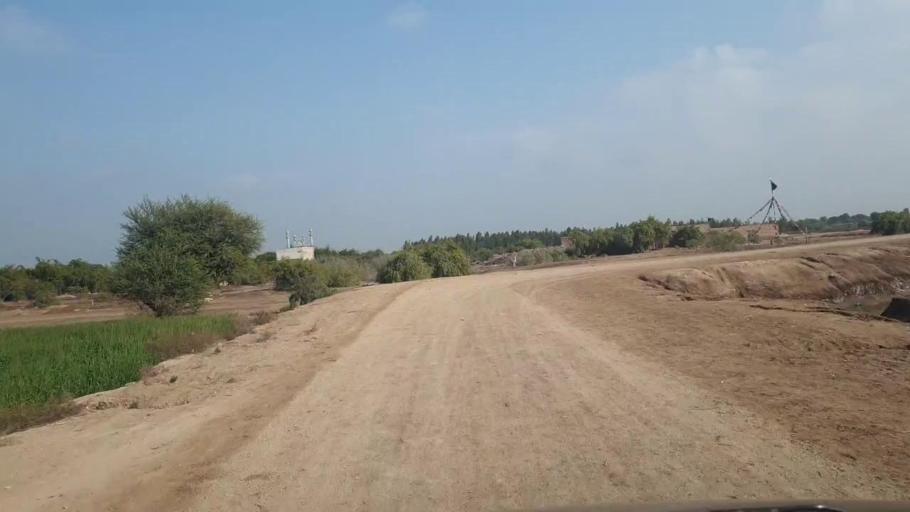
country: PK
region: Sindh
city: Shahdadpur
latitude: 25.9132
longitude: 68.6819
